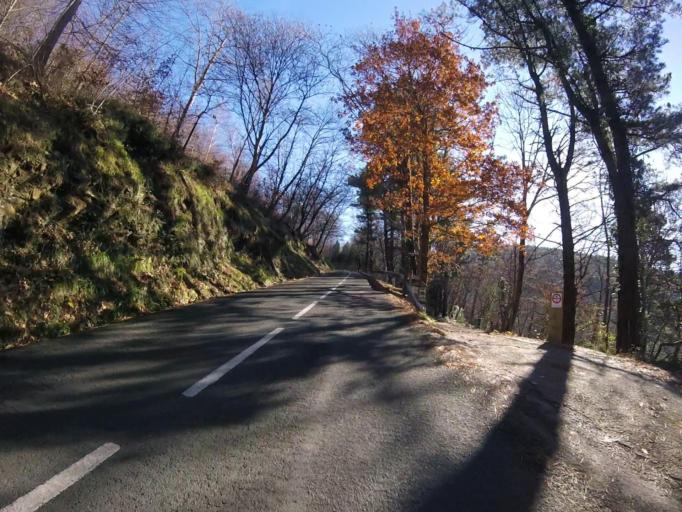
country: ES
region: Basque Country
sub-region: Provincia de Guipuzcoa
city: Irun
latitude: 43.3156
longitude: -1.7619
